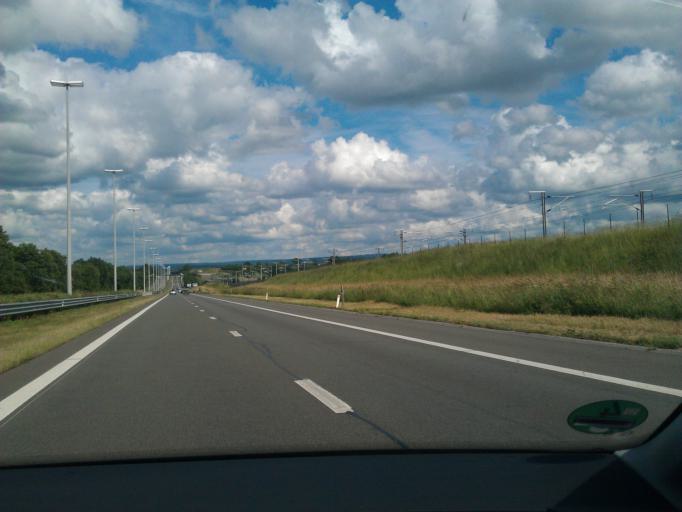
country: BE
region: Wallonia
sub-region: Province de Liege
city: Welkenraedt
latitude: 50.6495
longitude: 5.9443
